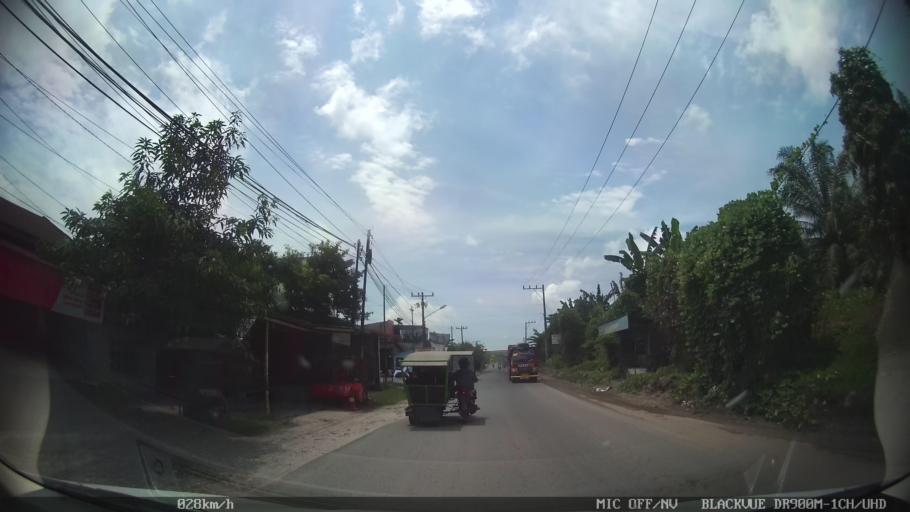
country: ID
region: North Sumatra
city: Perbaungan
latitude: 3.5344
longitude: 98.8857
